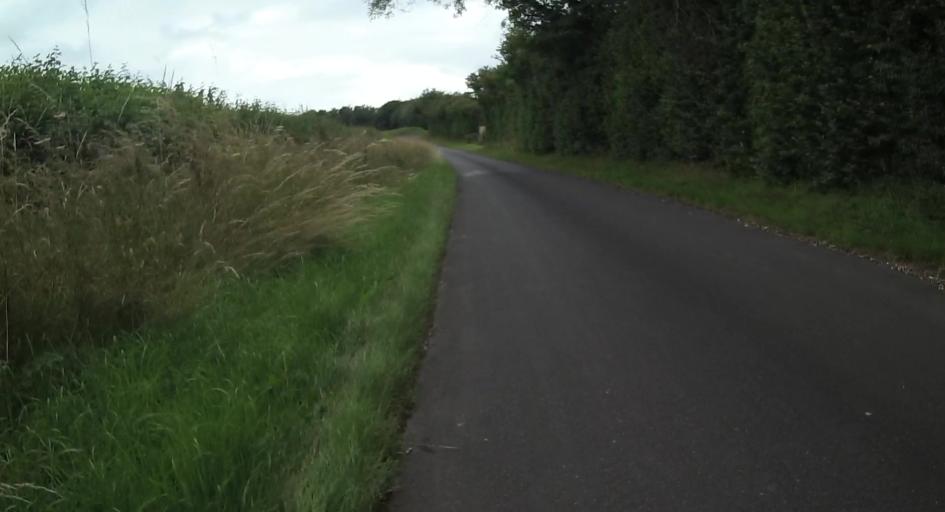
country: GB
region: England
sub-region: Hampshire
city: Swanmore
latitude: 51.0195
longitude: -1.1807
